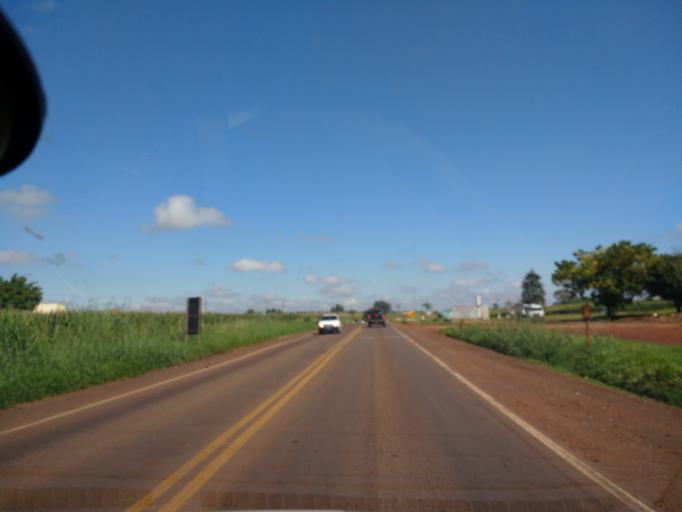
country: BR
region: Parana
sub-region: Terra Boa
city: Terra Boa
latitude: -23.6315
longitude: -52.4623
